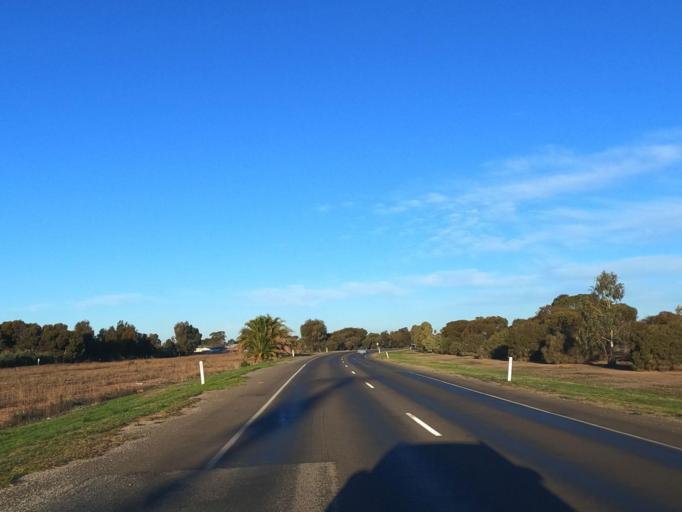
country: AU
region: Victoria
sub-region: Swan Hill
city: Swan Hill
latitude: -35.3371
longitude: 143.5368
